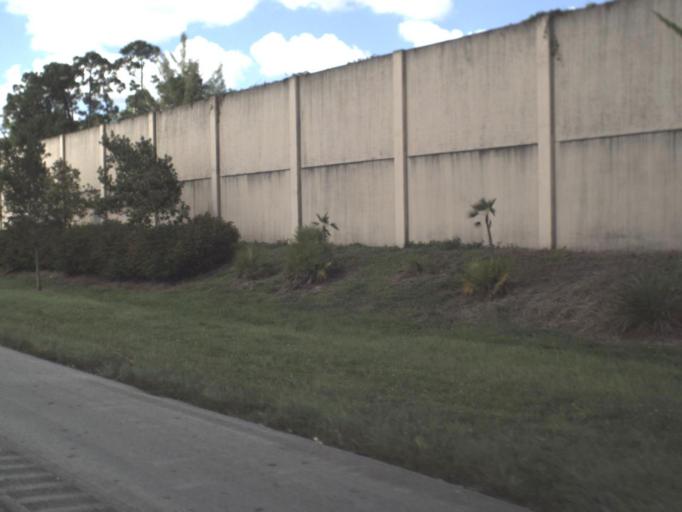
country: US
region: Florida
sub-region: Broward County
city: Parkland
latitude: 26.3009
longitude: -80.2238
